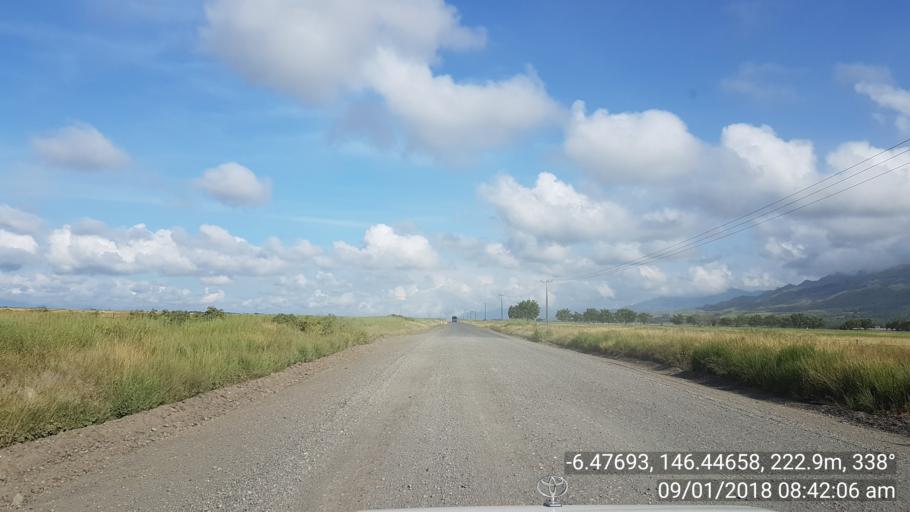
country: PG
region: Morobe
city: Lae
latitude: -6.4770
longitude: 146.4466
